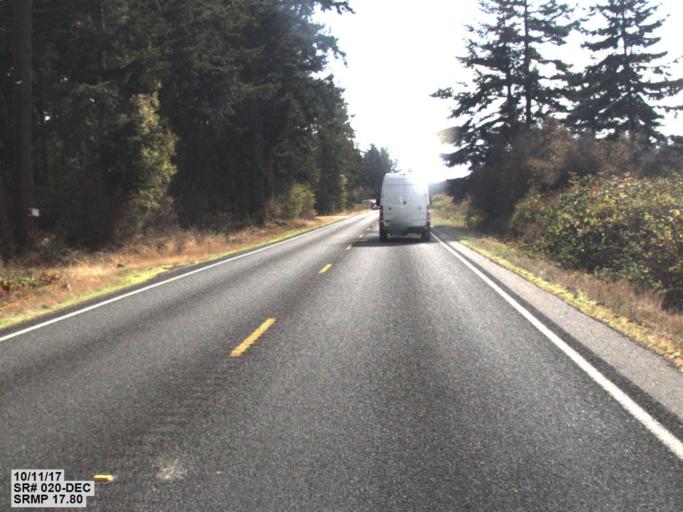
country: US
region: Washington
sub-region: Island County
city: Coupeville
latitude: 48.1870
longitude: -122.6266
